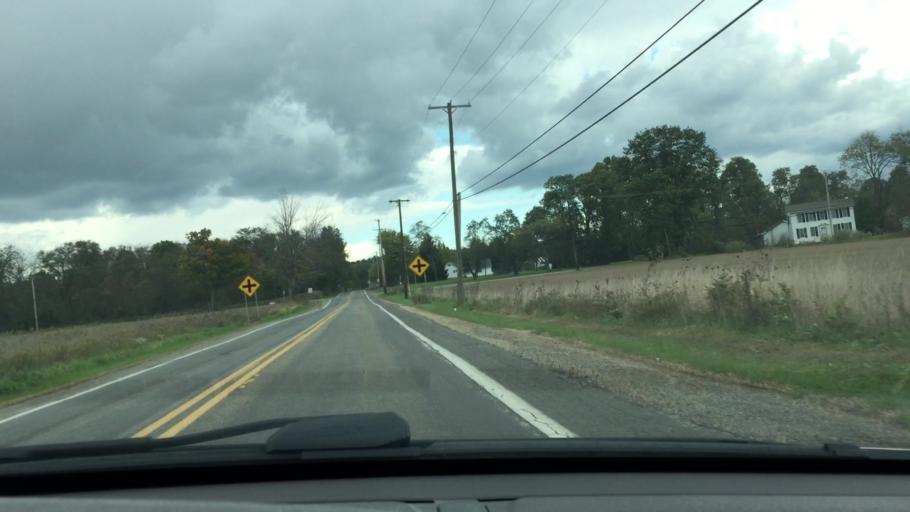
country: US
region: Pennsylvania
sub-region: Lawrence County
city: Oakwood
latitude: 41.0275
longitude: -80.4420
